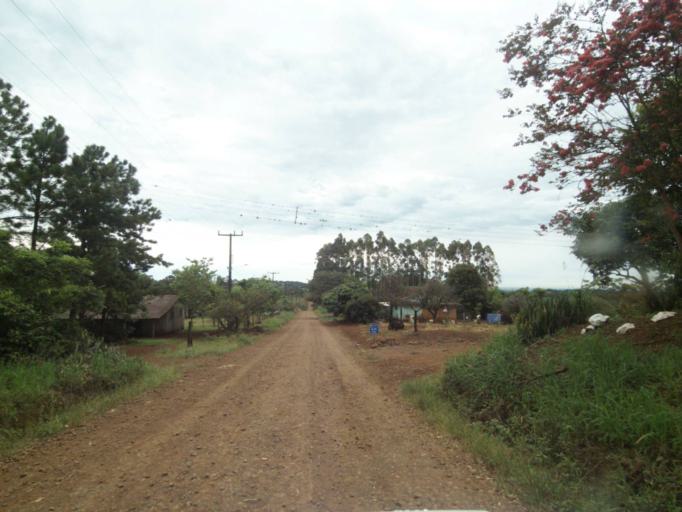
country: BR
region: Parana
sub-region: Guaraniacu
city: Guaraniacu
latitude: -24.9152
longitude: -52.9365
